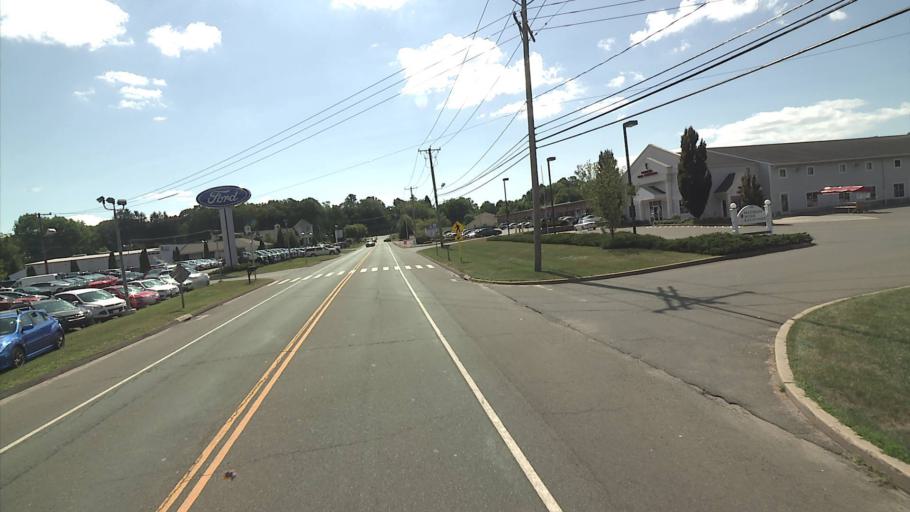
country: US
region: Connecticut
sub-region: New Haven County
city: Madison Center
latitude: 41.2821
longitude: -72.6318
